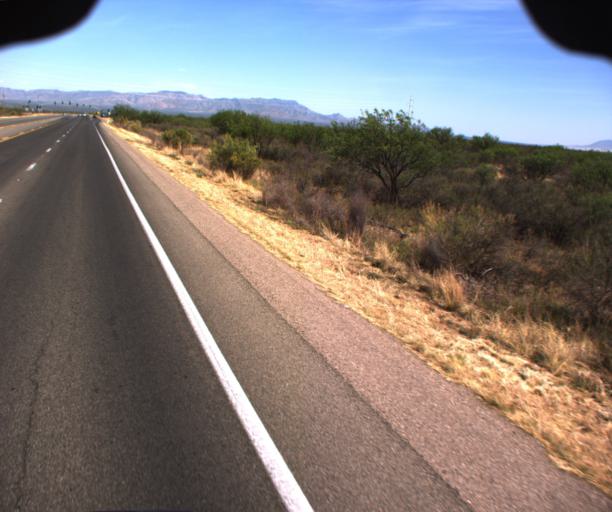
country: US
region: Arizona
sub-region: Cochise County
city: Sierra Vista Southeast
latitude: 31.5523
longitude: -110.1935
